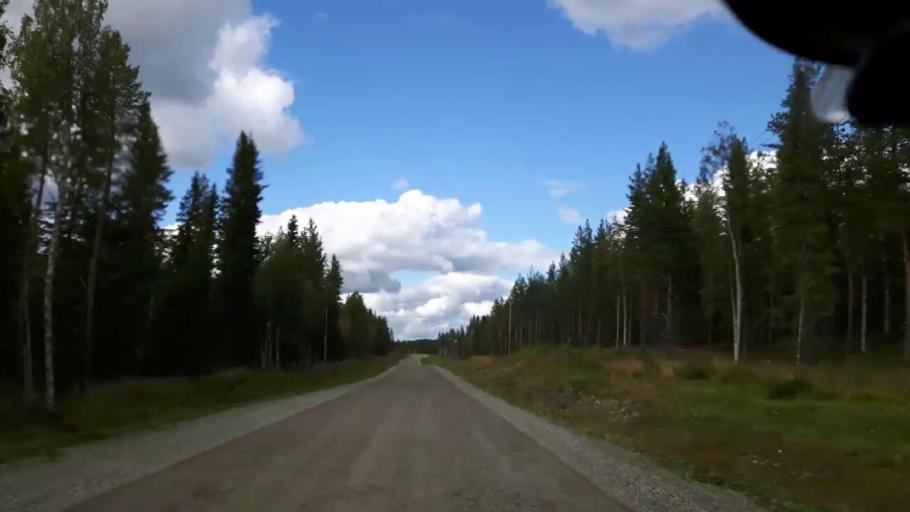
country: SE
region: Jaemtland
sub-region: Stroemsunds Kommun
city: Stroemsund
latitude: 63.3768
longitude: 15.5626
